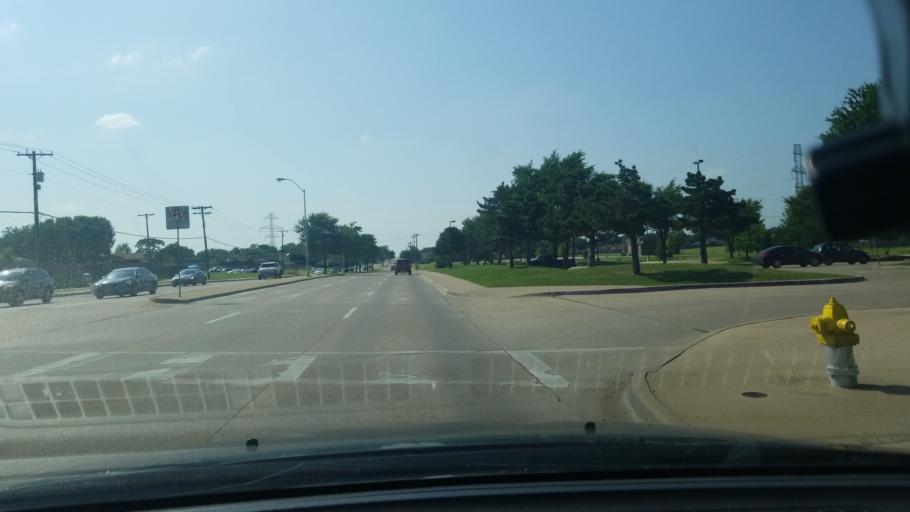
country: US
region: Texas
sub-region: Dallas County
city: Mesquite
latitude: 32.8180
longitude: -96.6151
